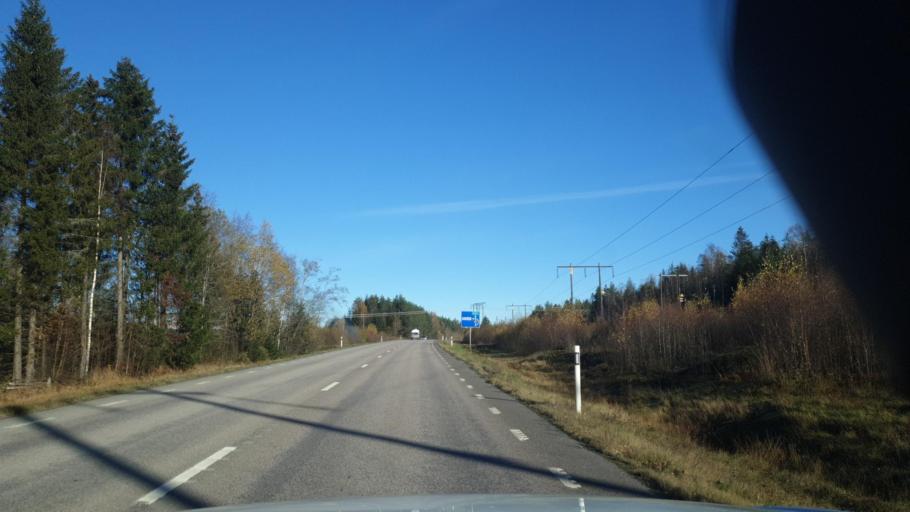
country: SE
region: Vaermland
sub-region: Karlstads Kommun
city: Edsvalla
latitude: 59.4139
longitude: 13.1849
